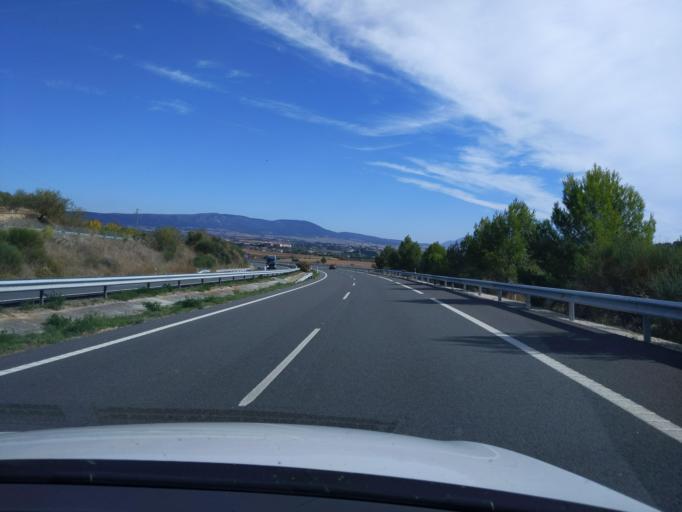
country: ES
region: Navarre
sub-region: Provincia de Navarra
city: Puente la Reina
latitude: 42.6667
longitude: -1.8347
